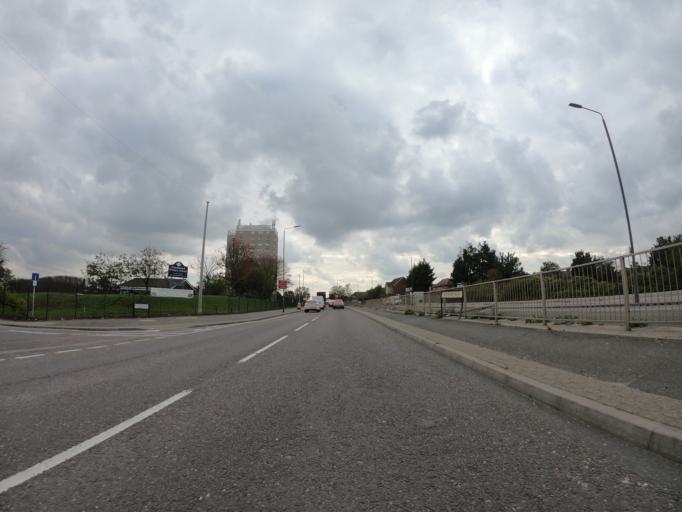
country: GB
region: England
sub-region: Greater London
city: Erith
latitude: 51.4715
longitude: 0.1810
